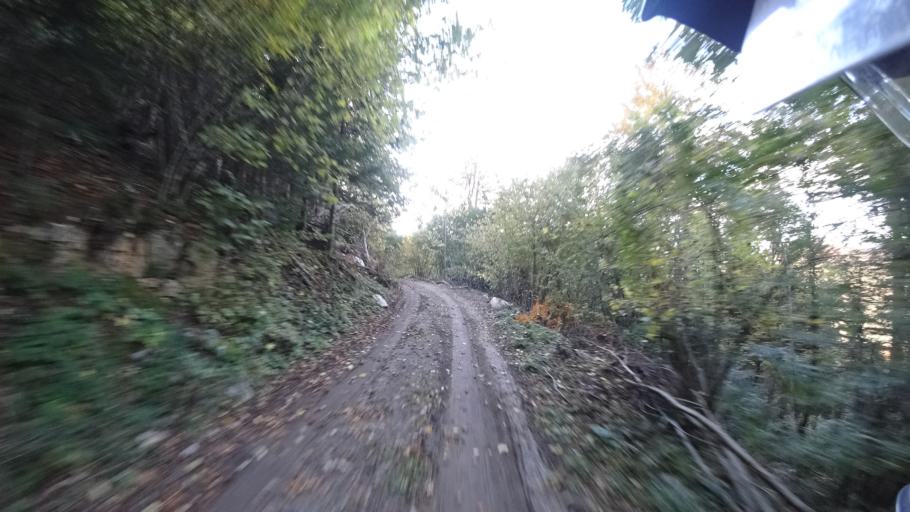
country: HR
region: Karlovacka
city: Plaski
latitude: 45.0315
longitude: 15.3805
